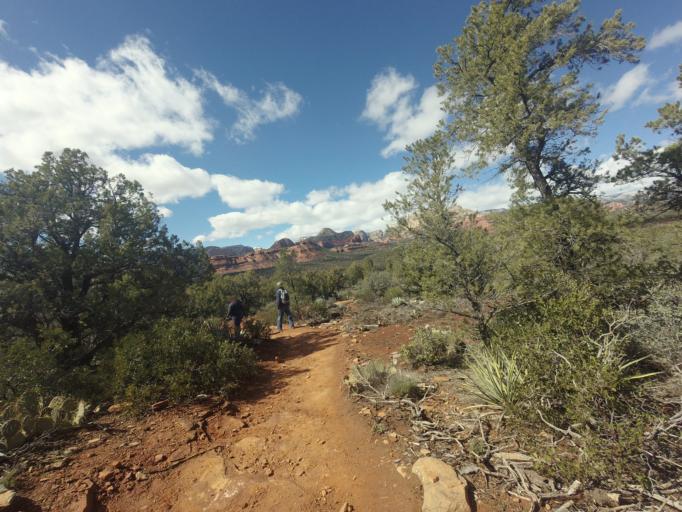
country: US
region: Arizona
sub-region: Yavapai County
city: West Sedona
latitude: 34.8973
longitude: -111.8219
